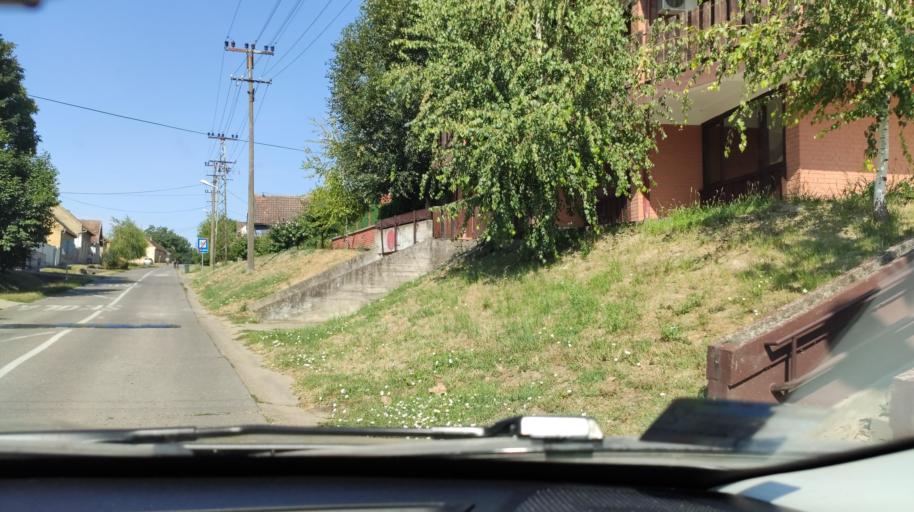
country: RS
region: Autonomna Pokrajina Vojvodina
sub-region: Severnobacki Okrug
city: Backa Topola
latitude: 45.8189
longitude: 19.6262
